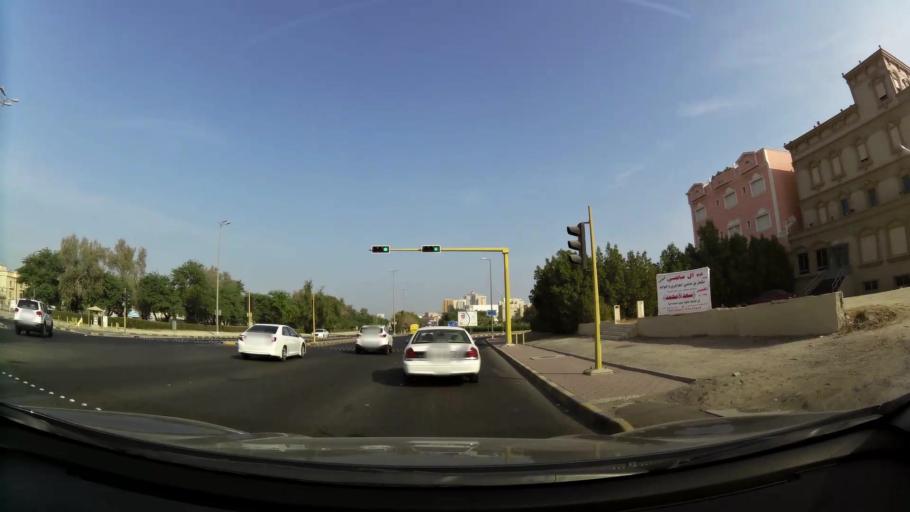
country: KW
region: Mubarak al Kabir
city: Mubarak al Kabir
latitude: 29.1748
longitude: 48.0877
